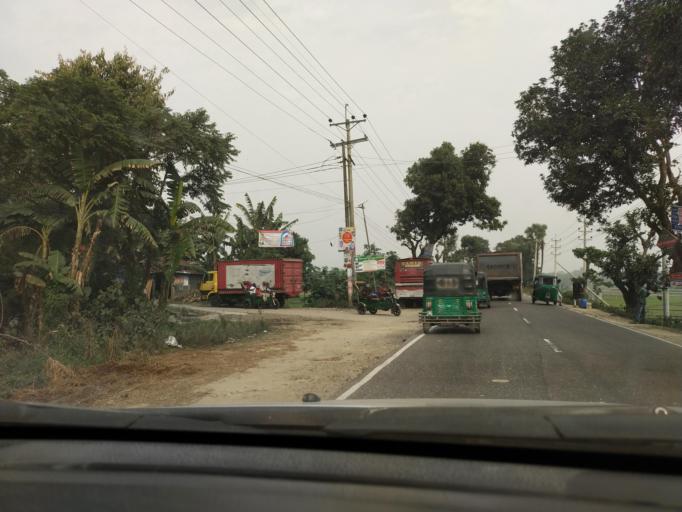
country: BD
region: Dhaka
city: Narsingdi
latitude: 24.0160
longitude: 90.7373
